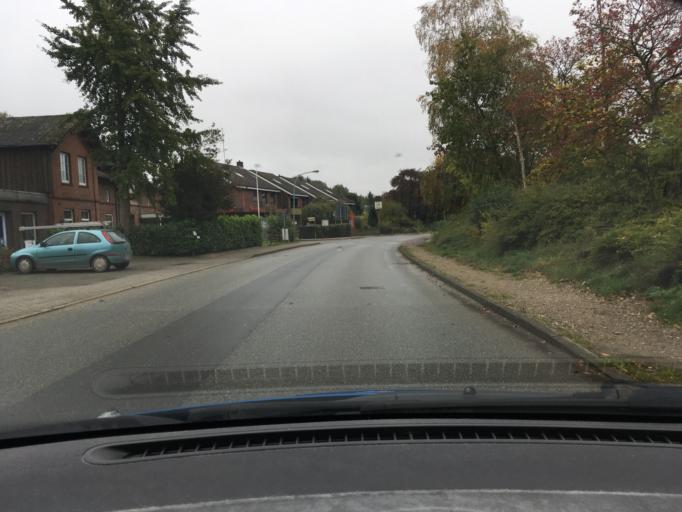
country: DE
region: Schleswig-Holstein
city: Bosau
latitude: 54.0893
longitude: 10.4768
